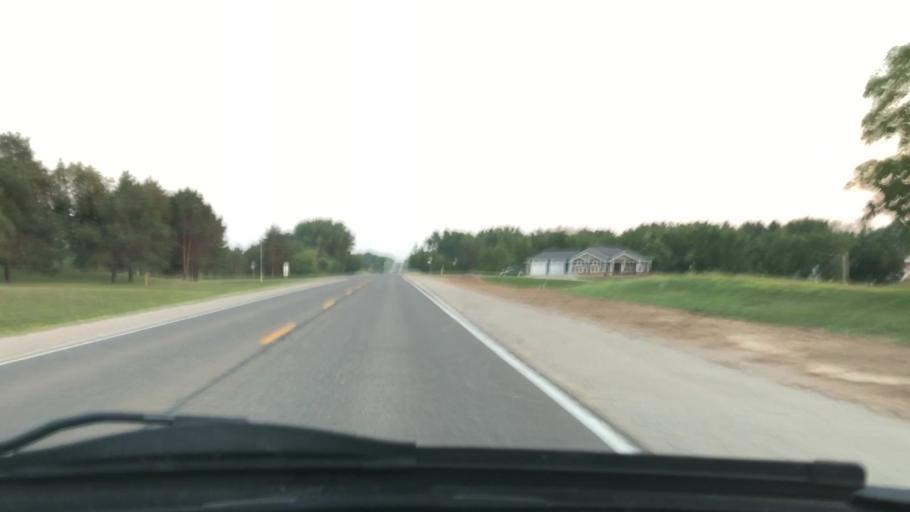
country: US
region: Iowa
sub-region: Henry County
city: Mount Pleasant
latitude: 40.9568
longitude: -91.5394
